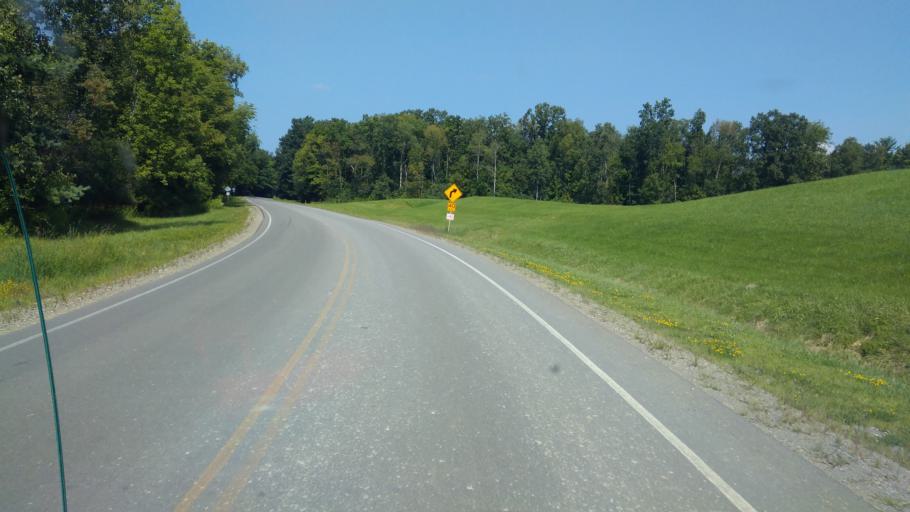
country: US
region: New York
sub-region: Allegany County
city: Belmont
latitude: 42.2614
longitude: -78.0381
